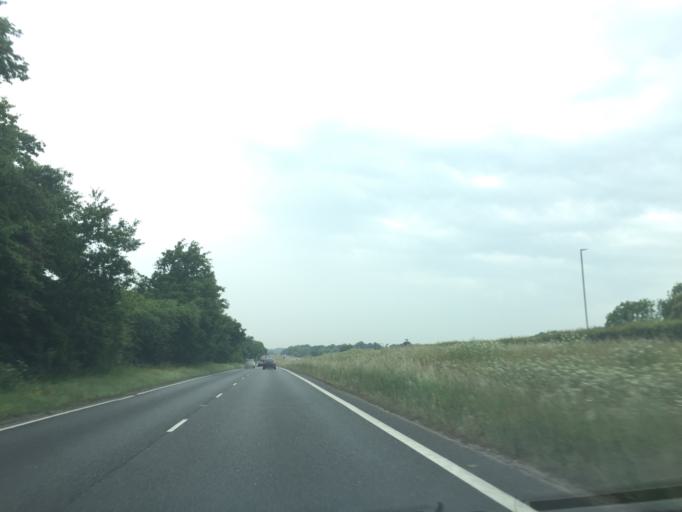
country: GB
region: England
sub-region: Poole
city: Poole
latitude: 50.7373
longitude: -2.0038
